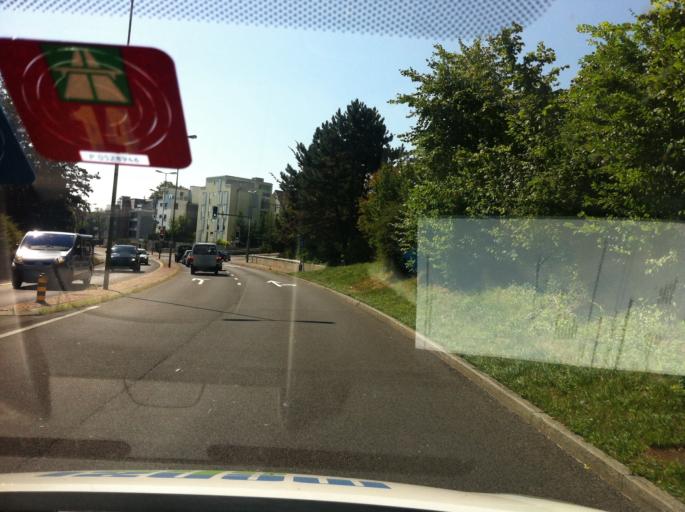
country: CH
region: Zurich
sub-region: Bezirk Horgen
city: Thalwil / Berg
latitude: 47.2929
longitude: 8.5566
